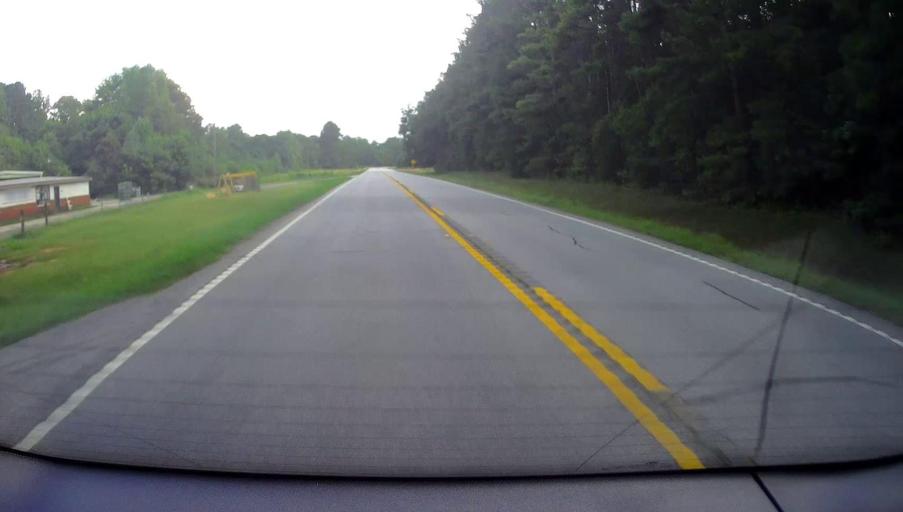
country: US
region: Georgia
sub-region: Meriwether County
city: Greenville
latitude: 33.0308
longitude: -84.5632
